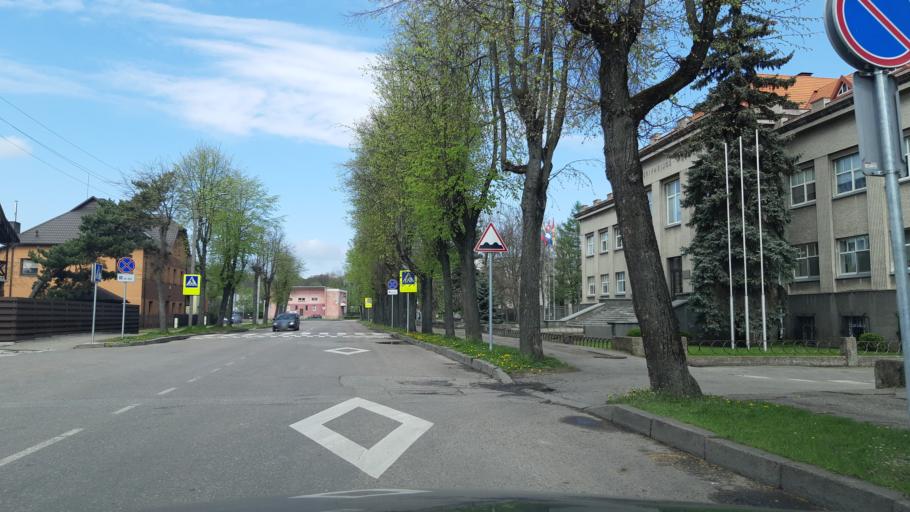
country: LT
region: Kauno apskritis
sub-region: Kaunas
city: Kaunas
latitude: 54.9077
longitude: 23.8798
